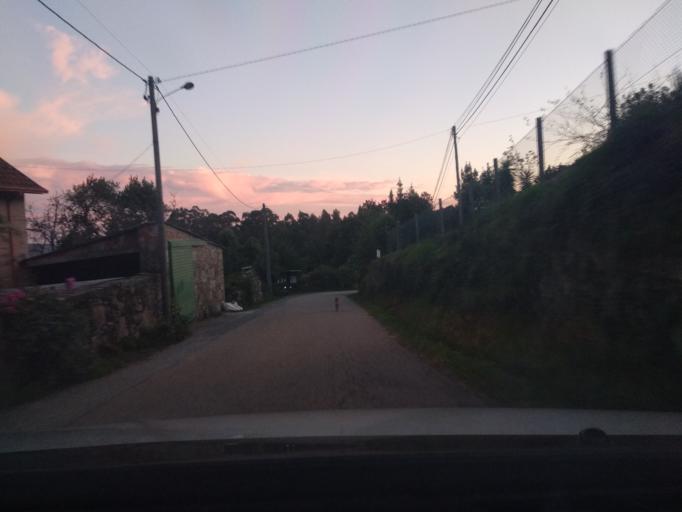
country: ES
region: Galicia
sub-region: Provincia de Pontevedra
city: Moana
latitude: 42.3030
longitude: -8.6994
